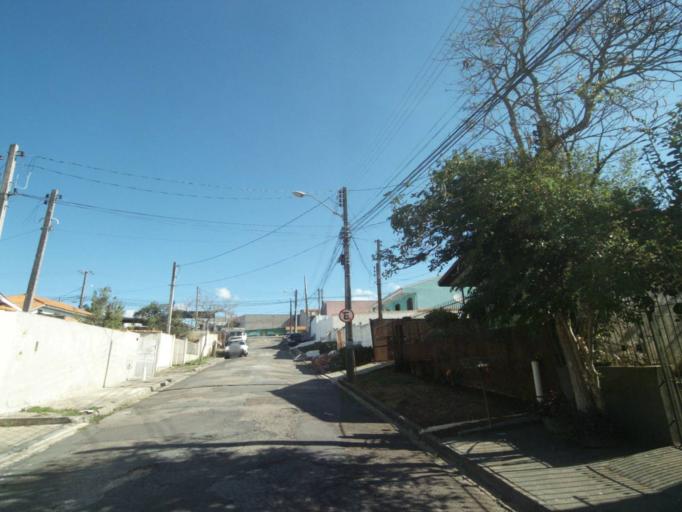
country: BR
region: Parana
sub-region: Curitiba
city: Curitiba
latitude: -25.3897
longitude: -49.2585
